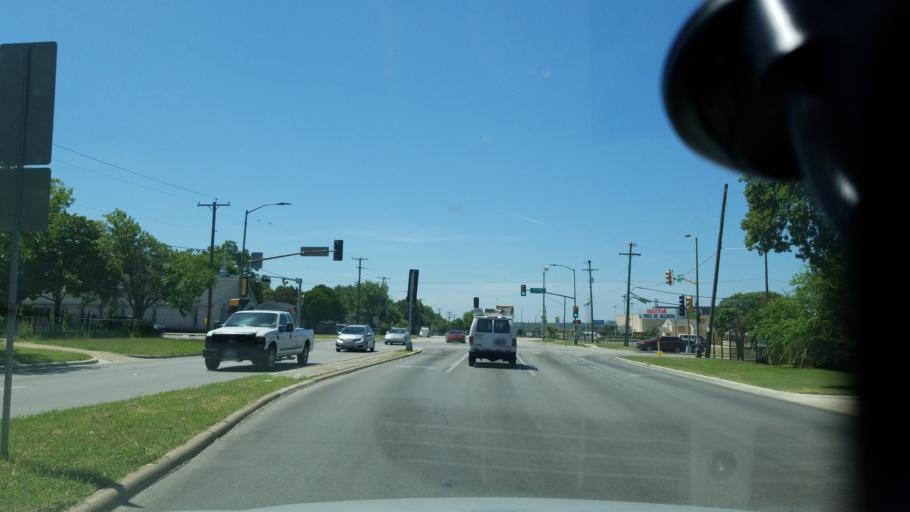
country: US
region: Texas
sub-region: Dallas County
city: Cockrell Hill
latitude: 32.7065
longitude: -96.8230
